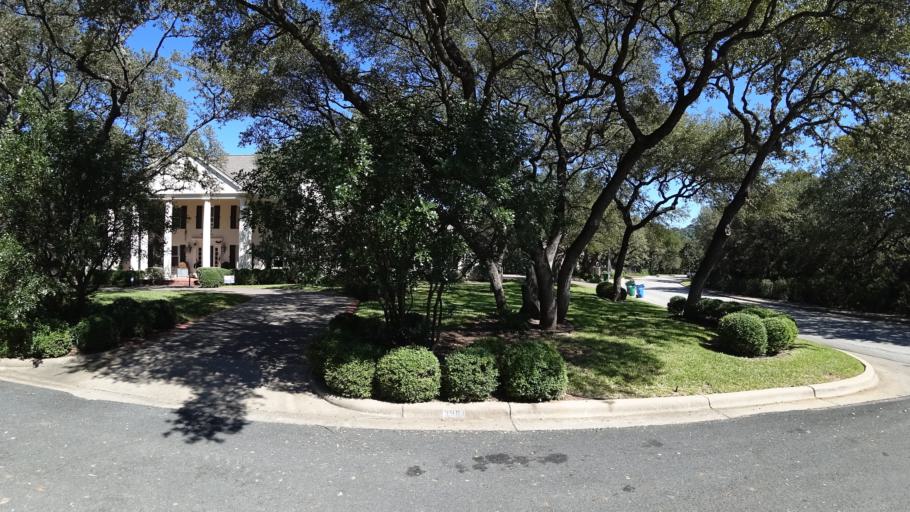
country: US
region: Texas
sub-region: Travis County
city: West Lake Hills
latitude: 30.3260
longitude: -97.7828
